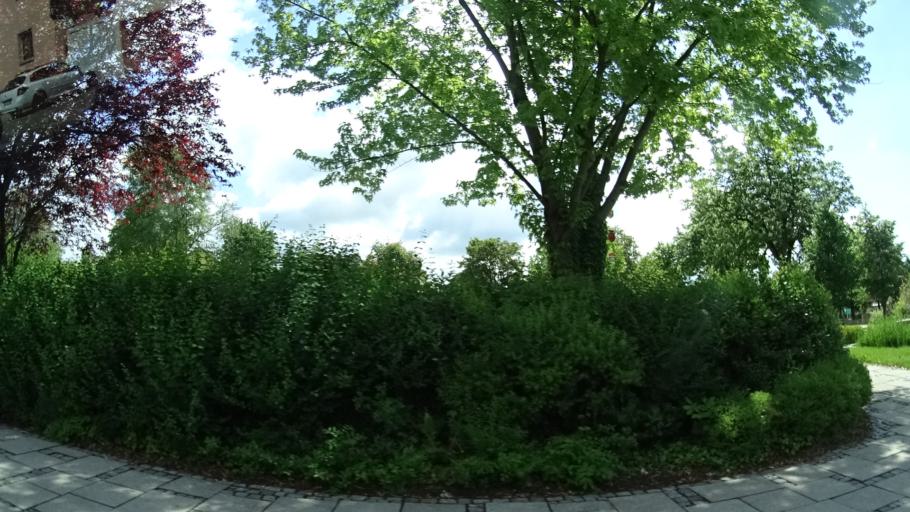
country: DE
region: Bavaria
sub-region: Regierungsbezirk Unterfranken
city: Mellrichstadt
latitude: 50.4309
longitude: 10.3042
